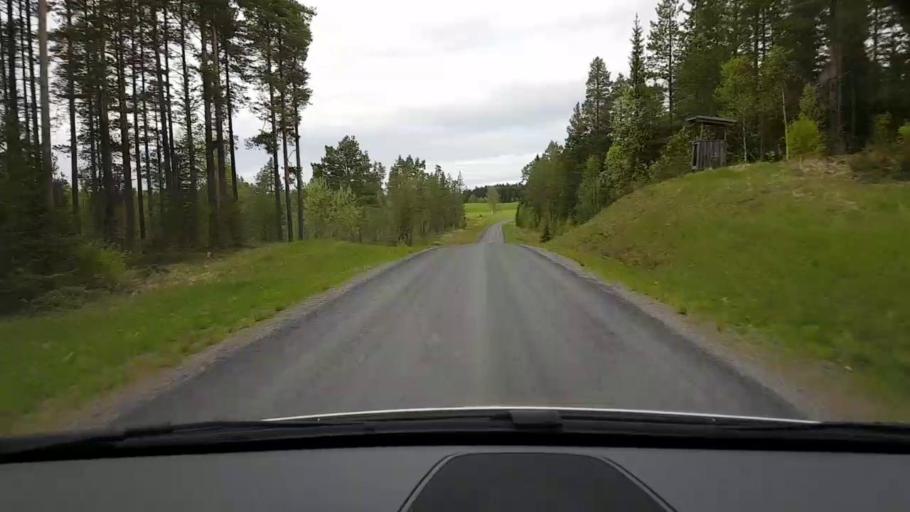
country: SE
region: Jaemtland
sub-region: Krokoms Kommun
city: Krokom
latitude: 63.3057
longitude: 14.3956
